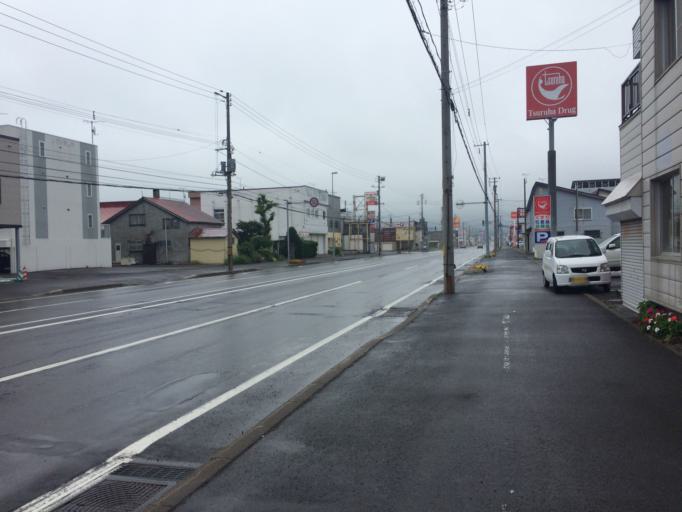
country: JP
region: Hokkaido
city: Niseko Town
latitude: 42.8963
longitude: 140.7521
